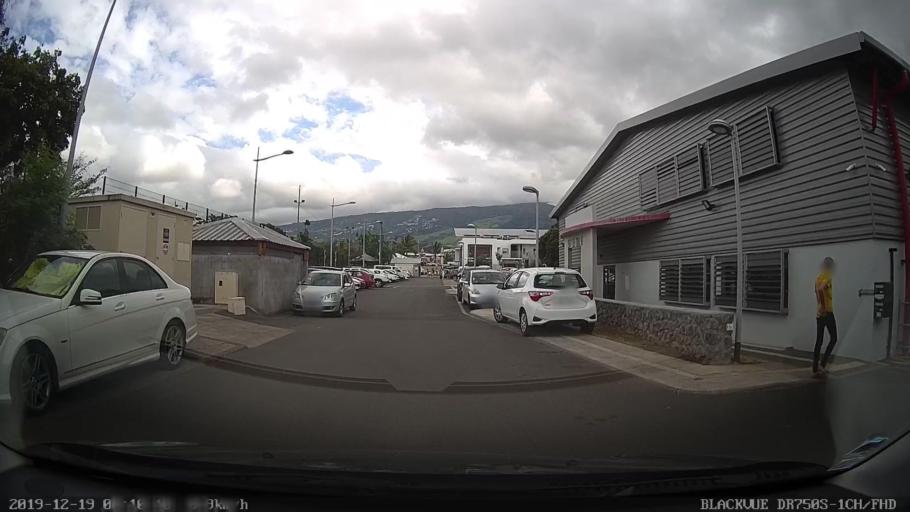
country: RE
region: Reunion
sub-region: Reunion
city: Sainte-Marie
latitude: -20.8987
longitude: 55.5037
